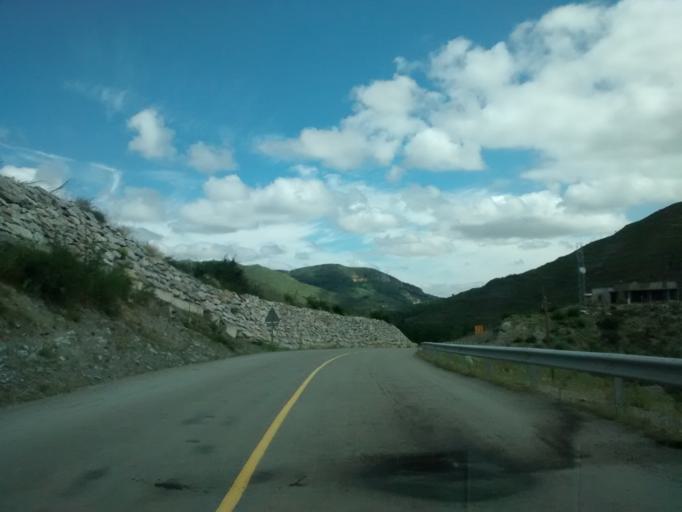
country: ES
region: La Rioja
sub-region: Provincia de La Rioja
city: Terroba
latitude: 42.2675
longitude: -2.4335
